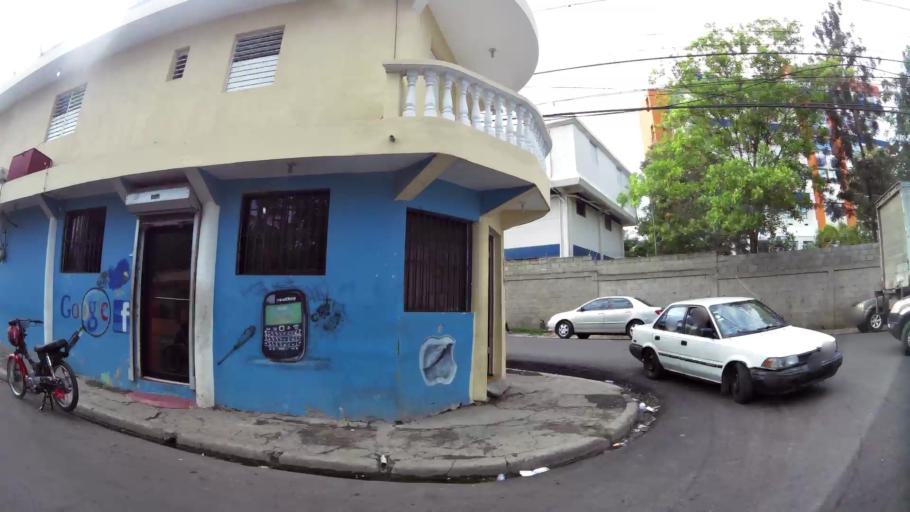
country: DO
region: Santiago
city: Santiago de los Caballeros
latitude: 19.4265
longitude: -70.6716
